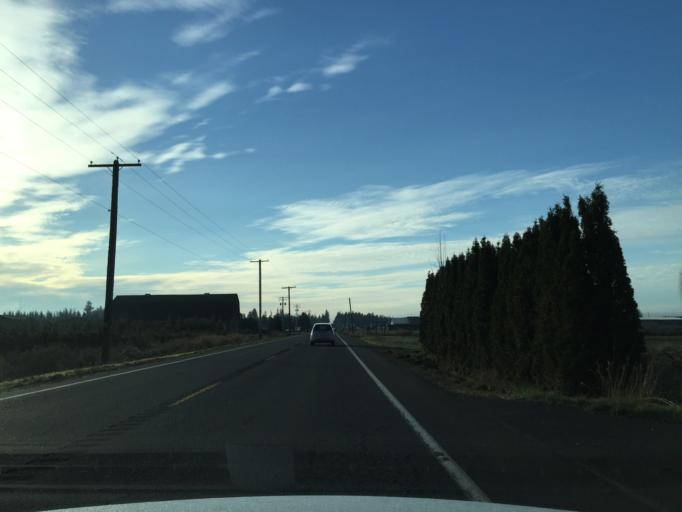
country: US
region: Washington
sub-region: Whatcom County
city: Lynden
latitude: 48.9527
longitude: -122.4853
